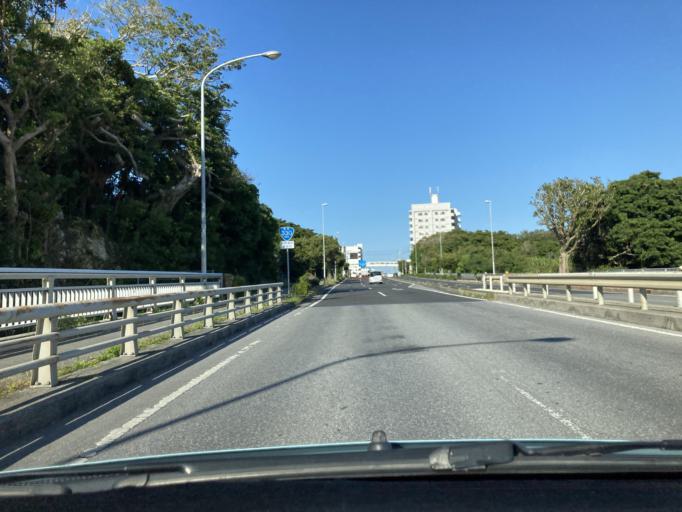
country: JP
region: Okinawa
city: Ginowan
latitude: 26.2527
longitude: 127.7514
